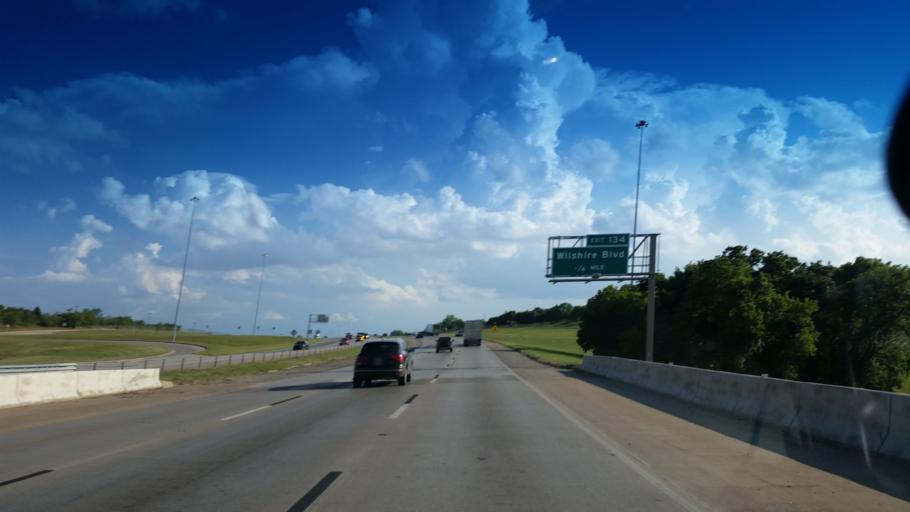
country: US
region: Oklahoma
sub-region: Oklahoma County
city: Spencer
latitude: 35.5657
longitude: -97.4516
